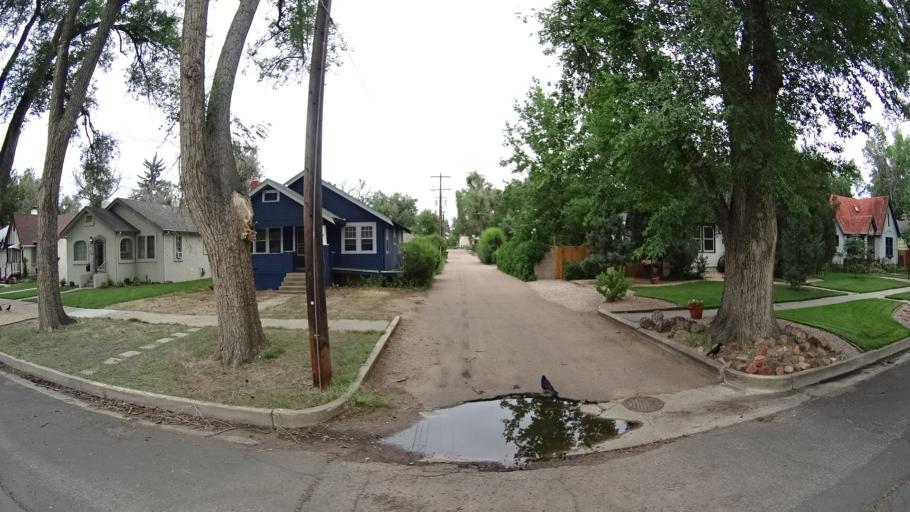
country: US
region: Colorado
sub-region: El Paso County
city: Colorado Springs
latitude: 38.8447
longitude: -104.8069
